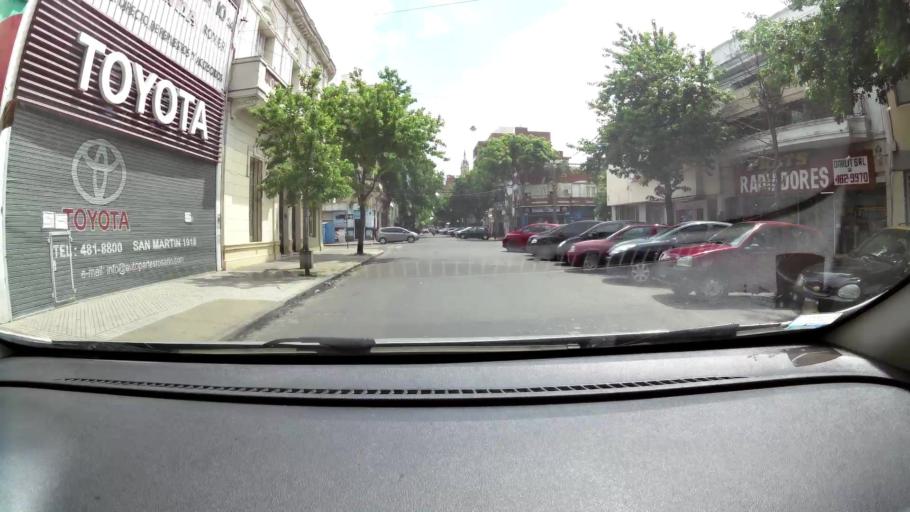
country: AR
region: Santa Fe
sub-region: Departamento de Rosario
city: Rosario
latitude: -32.9601
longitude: -60.6401
